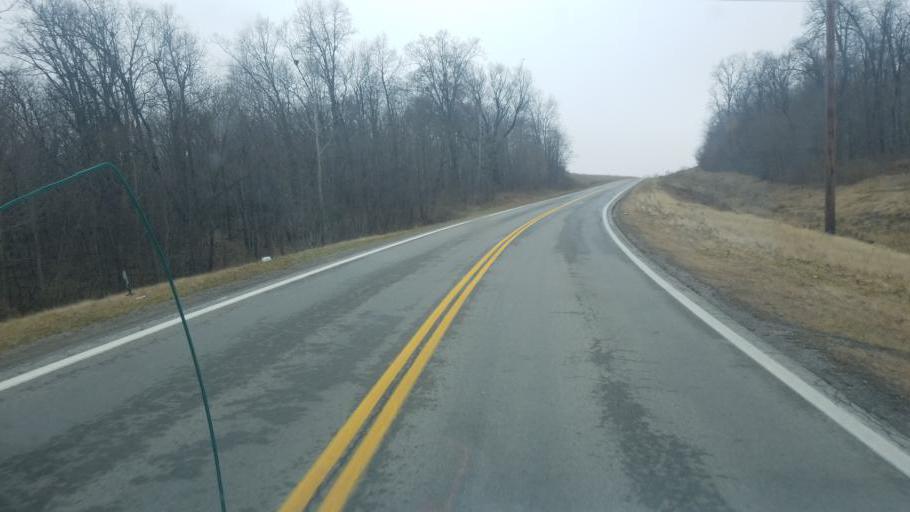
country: US
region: Ohio
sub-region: Champaign County
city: North Lewisburg
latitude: 40.3188
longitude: -83.5887
